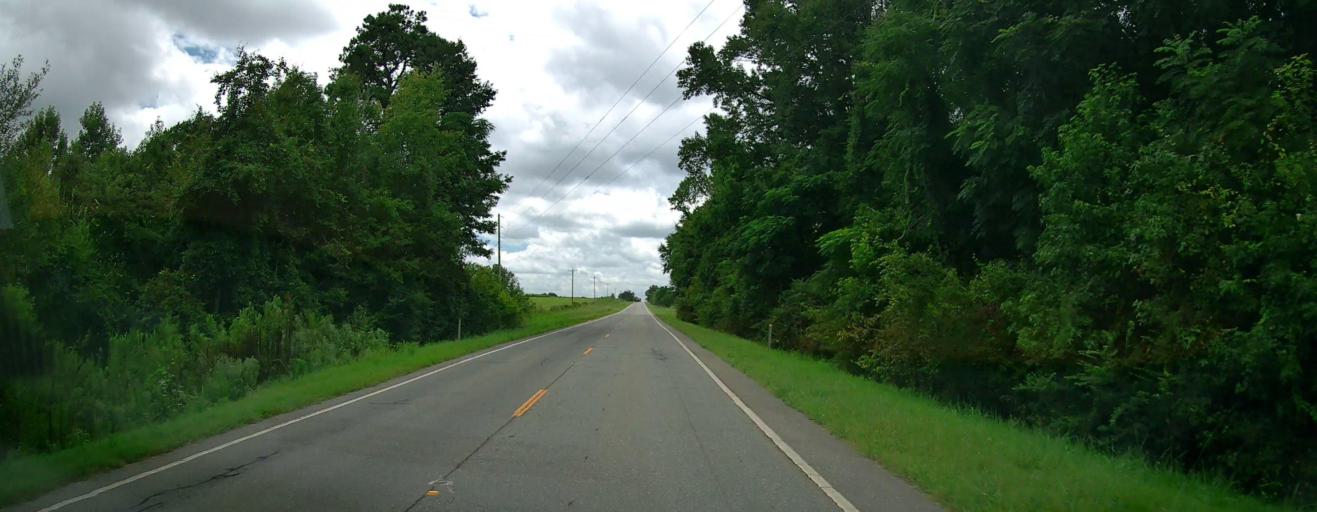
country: US
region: Georgia
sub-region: Wilcox County
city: Rochelle
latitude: 32.0158
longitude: -83.5573
